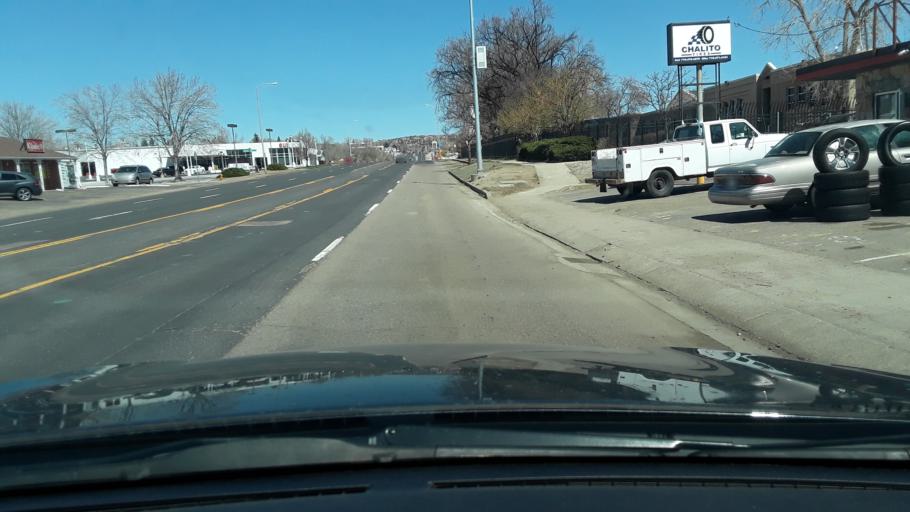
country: US
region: Colorado
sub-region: El Paso County
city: Colorado Springs
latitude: 38.8416
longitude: -104.7758
